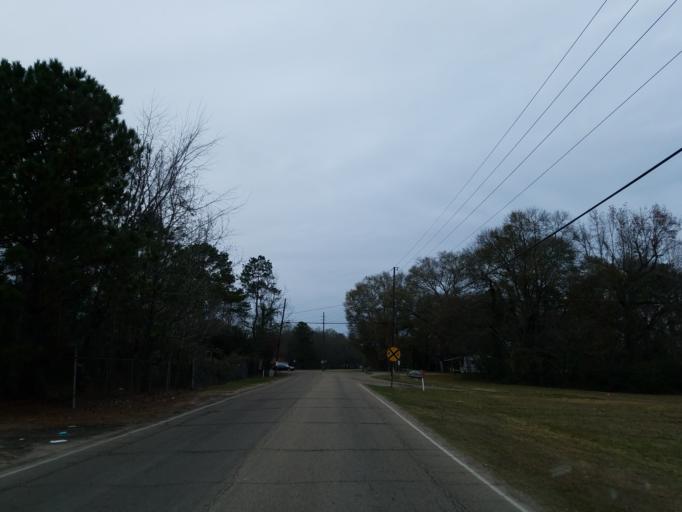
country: US
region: Mississippi
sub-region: Forrest County
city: Hattiesburg
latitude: 31.3153
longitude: -89.2827
